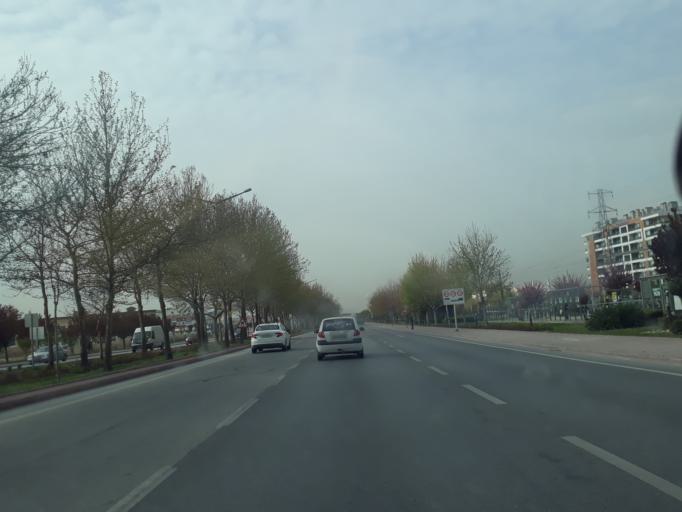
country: TR
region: Konya
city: Selcuklu
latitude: 37.9725
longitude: 32.5158
